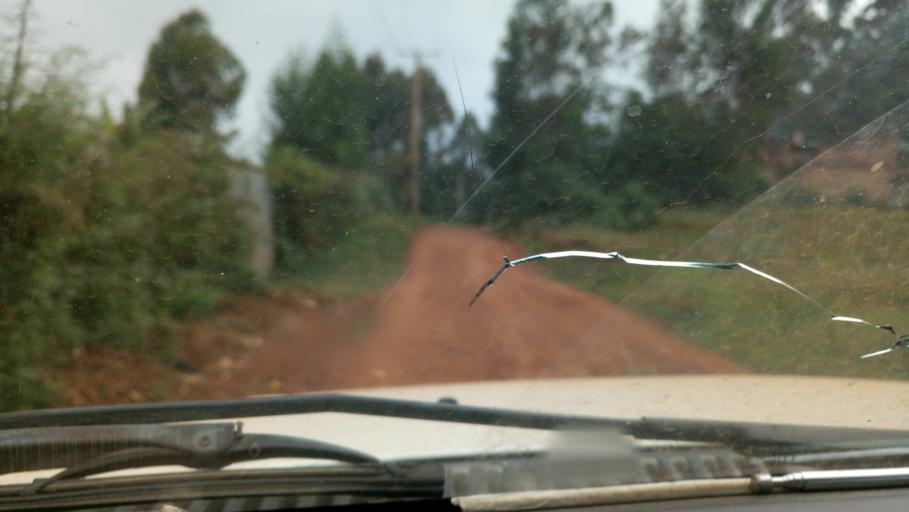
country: KE
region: Murang'a District
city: Kangema
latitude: -0.6822
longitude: 36.9287
